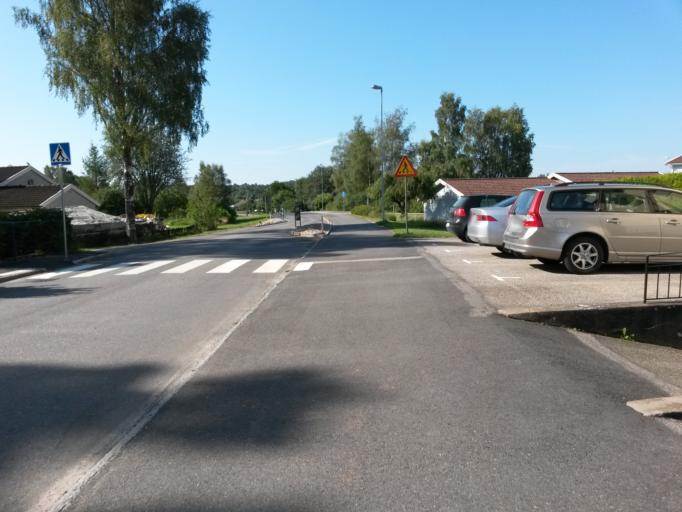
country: SE
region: Vaestra Goetaland
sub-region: Vargarda Kommun
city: Vargarda
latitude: 58.0260
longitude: 12.8131
